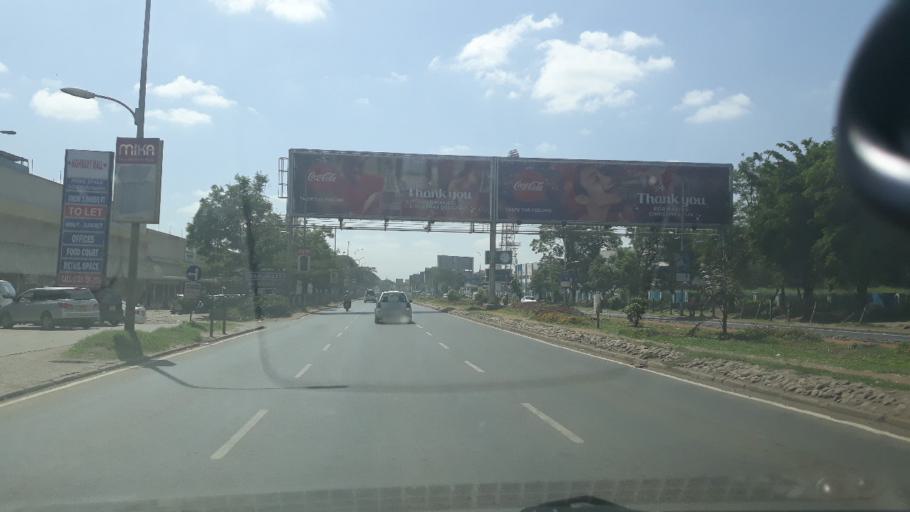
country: KE
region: Nairobi Area
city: Nairobi
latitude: -1.3009
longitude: 36.8247
